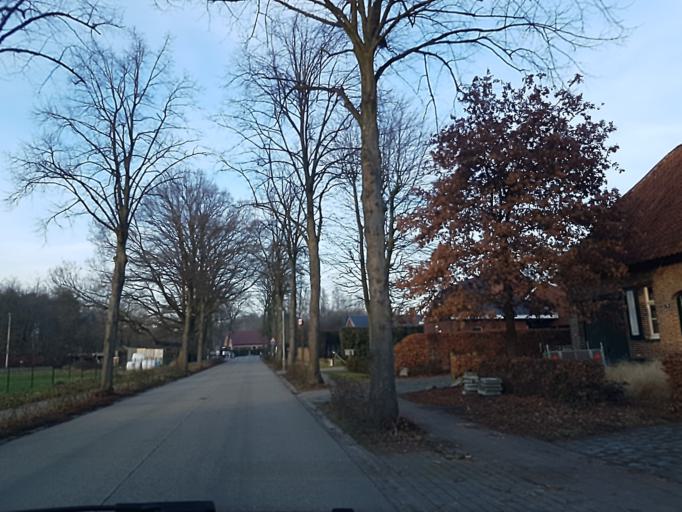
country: BE
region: Flanders
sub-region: Provincie Antwerpen
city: Zandhoven
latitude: 51.2467
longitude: 4.6466
